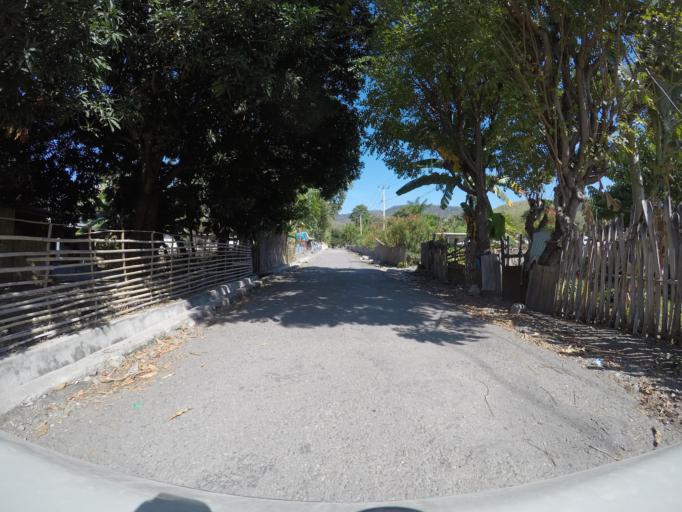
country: TL
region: Liquica
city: Maubara
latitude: -8.6120
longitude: 125.2052
